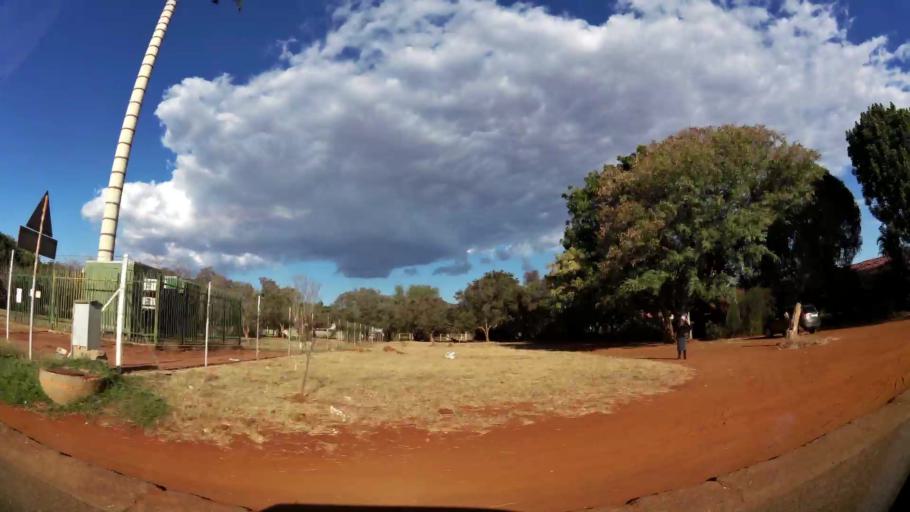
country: ZA
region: Limpopo
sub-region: Waterberg District Municipality
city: Mokopane
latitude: -24.2043
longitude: 29.0002
